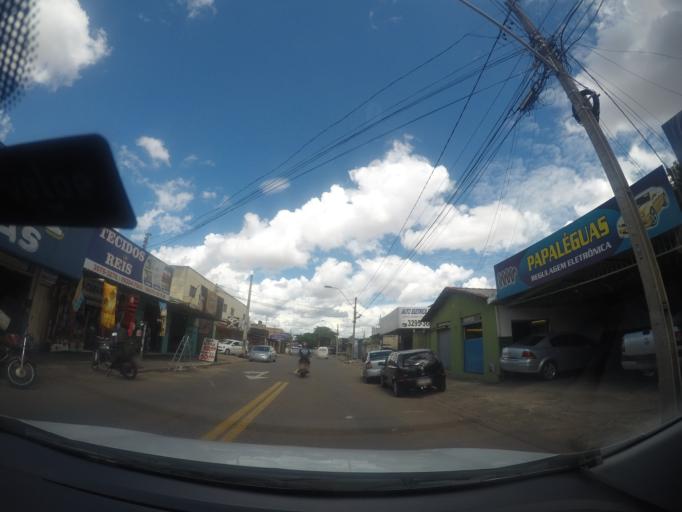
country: BR
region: Goias
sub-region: Goiania
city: Goiania
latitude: -16.6630
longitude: -49.3028
